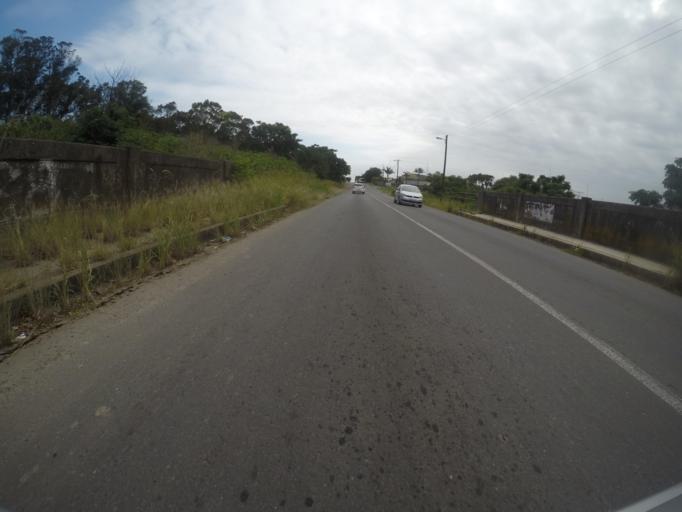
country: ZA
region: Eastern Cape
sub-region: Buffalo City Metropolitan Municipality
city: East London
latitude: -32.9904
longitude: 27.8890
